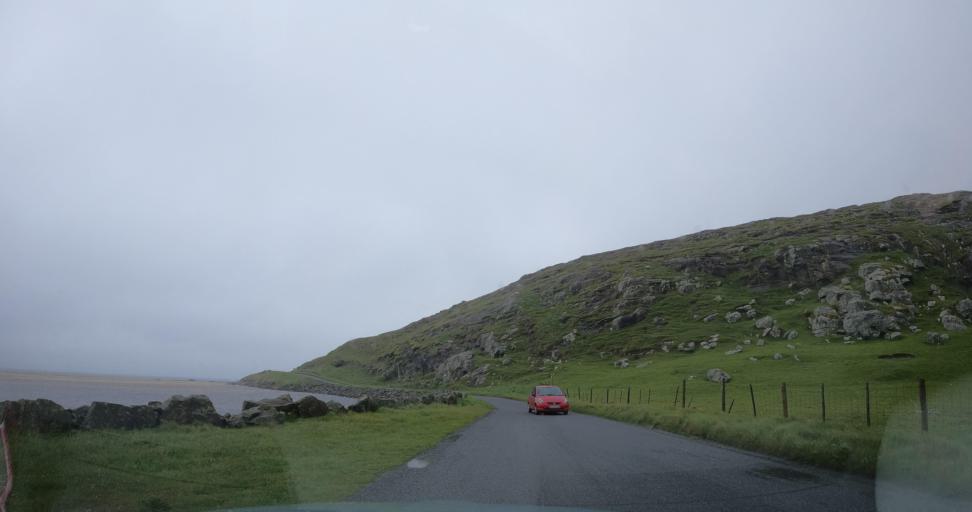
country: GB
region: Scotland
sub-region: Eilean Siar
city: Barra
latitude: 56.9877
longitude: -7.5081
